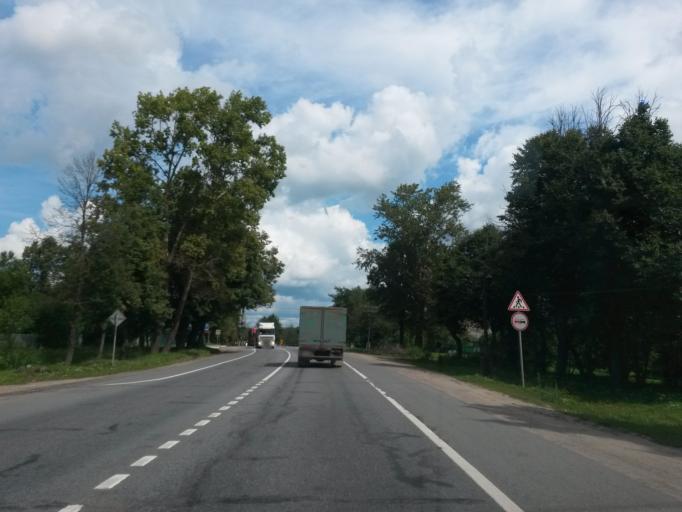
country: RU
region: Jaroslavl
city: Pereslavl'-Zalesskiy
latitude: 56.6528
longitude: 38.6991
